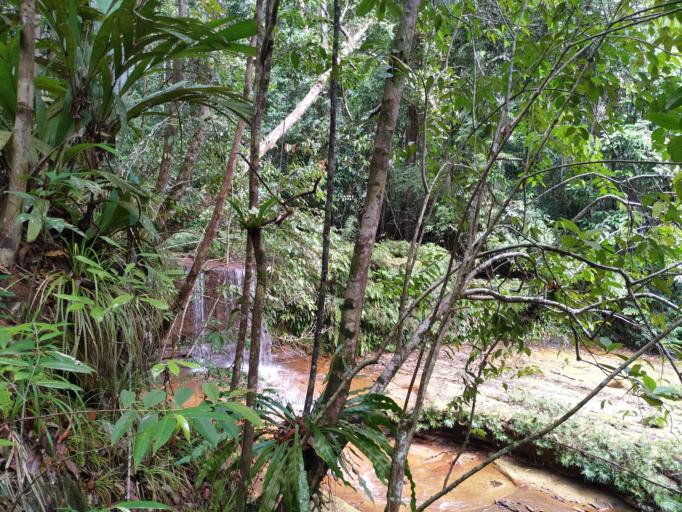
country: MY
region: Sarawak
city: Miri
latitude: 4.2018
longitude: 114.0450
